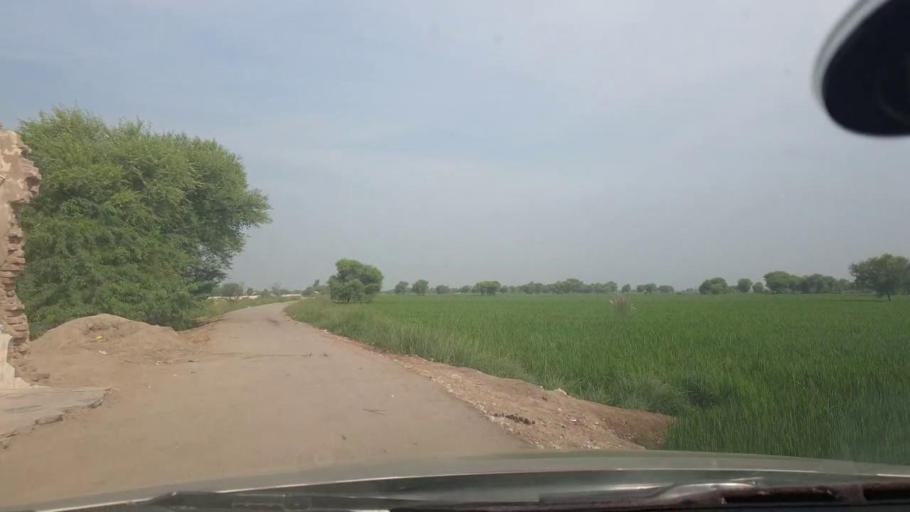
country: PK
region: Sindh
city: Jacobabad
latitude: 28.2888
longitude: 68.4824
